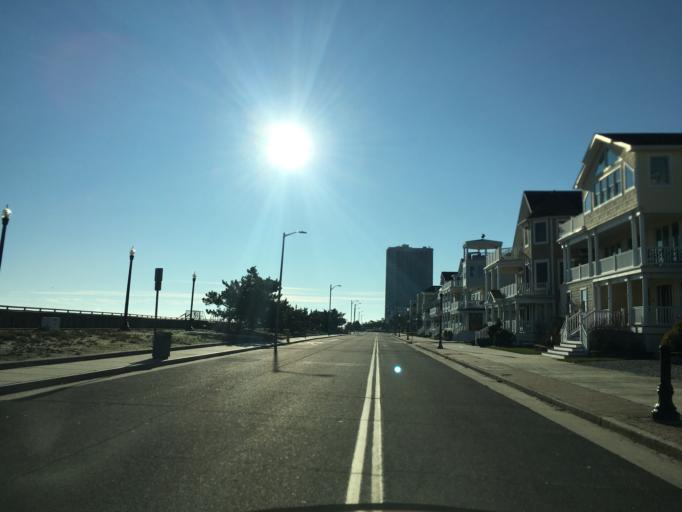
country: US
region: New Jersey
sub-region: Atlantic County
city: Atlantic City
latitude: 39.3754
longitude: -74.4161
